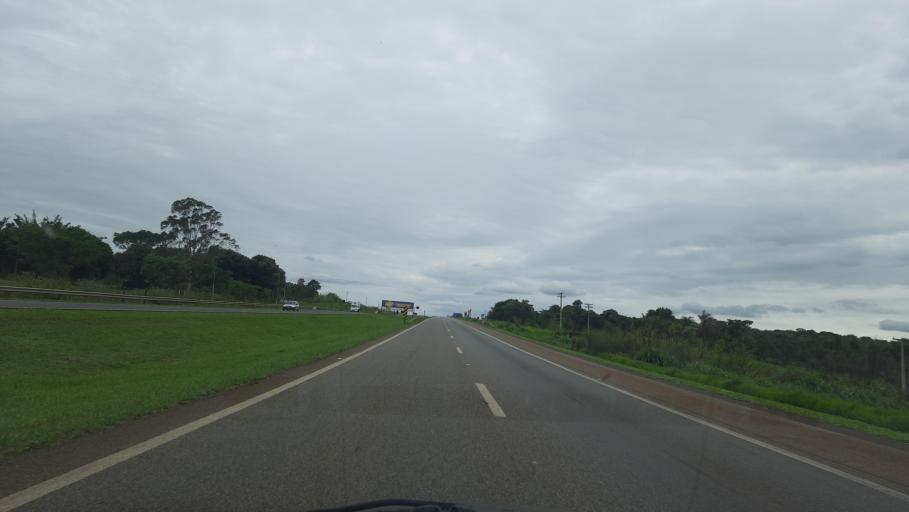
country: BR
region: Sao Paulo
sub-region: Aguai
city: Aguai
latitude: -22.1778
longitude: -46.9890
